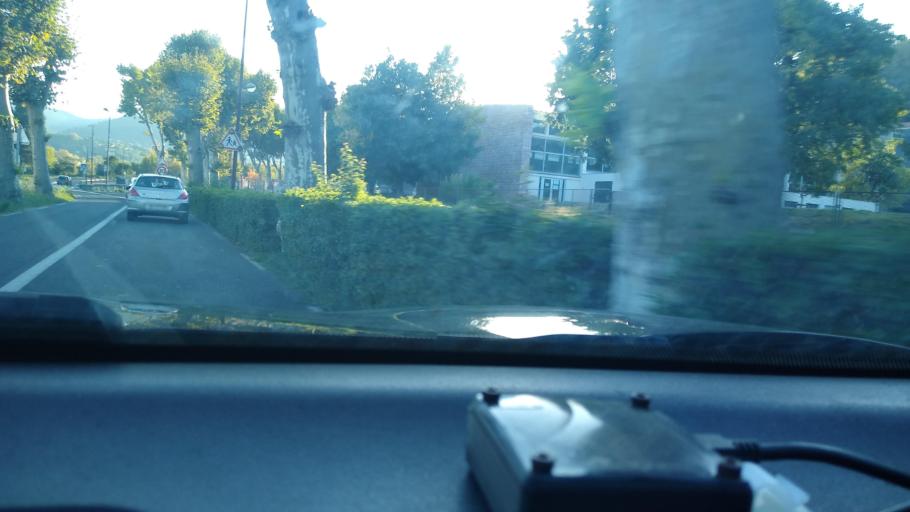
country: FR
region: Languedoc-Roussillon
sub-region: Departement des Pyrenees-Orientales
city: Prades
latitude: 42.6242
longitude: 2.4183
